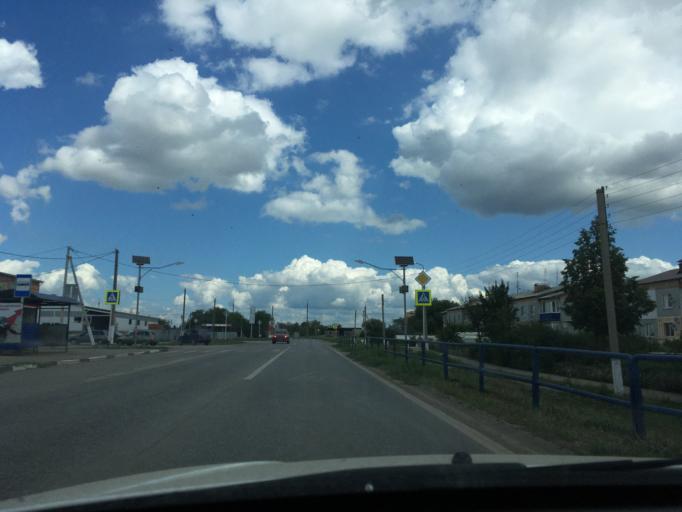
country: RU
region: Samara
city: Bezenchuk
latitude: 52.9940
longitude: 49.4378
